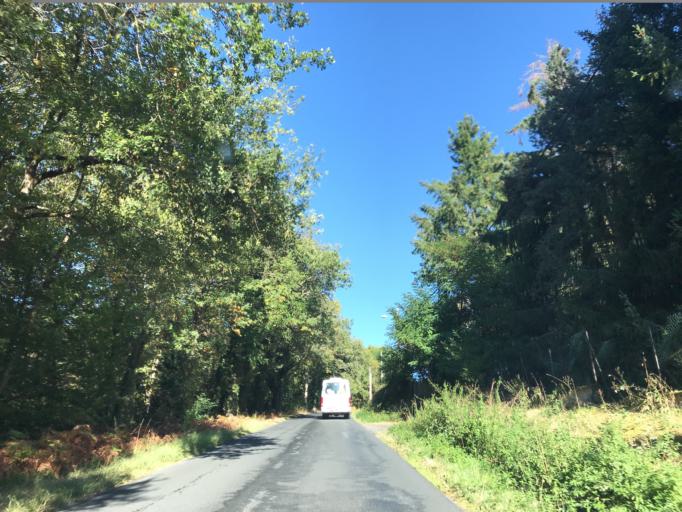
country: FR
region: Auvergne
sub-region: Departement du Puy-de-Dome
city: Courpiere
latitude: 45.7533
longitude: 3.5596
